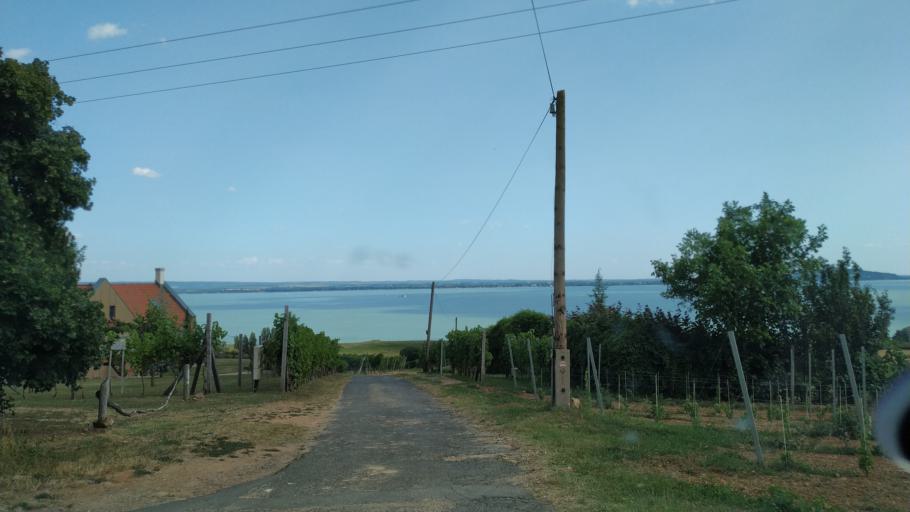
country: HU
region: Veszprem
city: Badacsonytomaj
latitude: 46.8092
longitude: 17.5413
